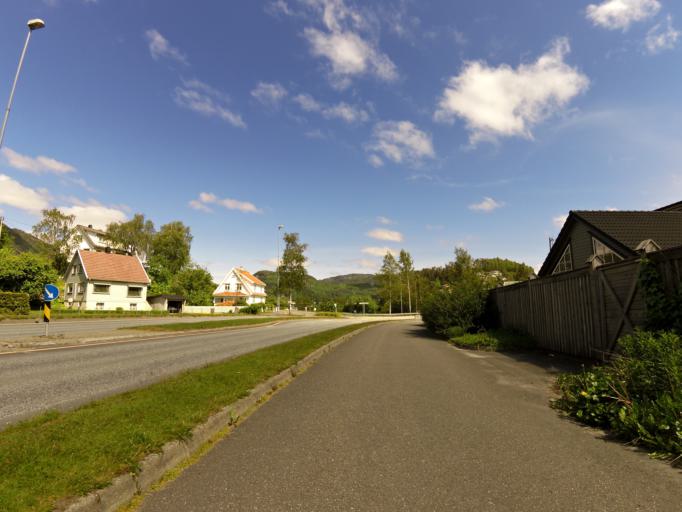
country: NO
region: Vest-Agder
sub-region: Kvinesdal
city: Liknes
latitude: 58.3108
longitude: 6.9591
